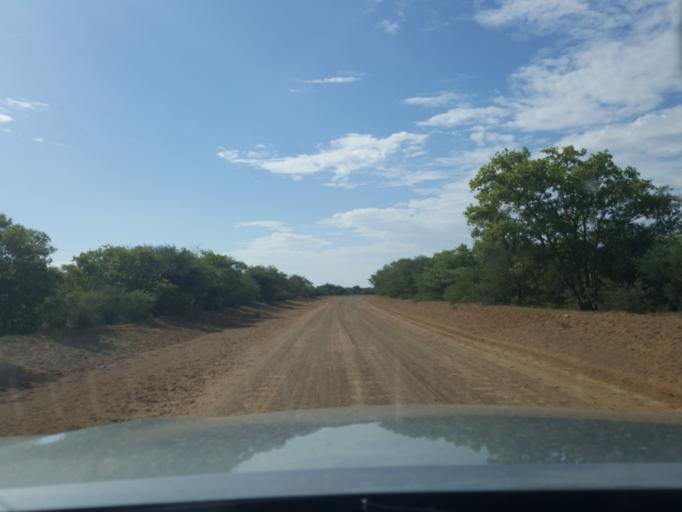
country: BW
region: Kweneng
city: Khudumelapye
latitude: -23.5311
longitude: 24.7242
